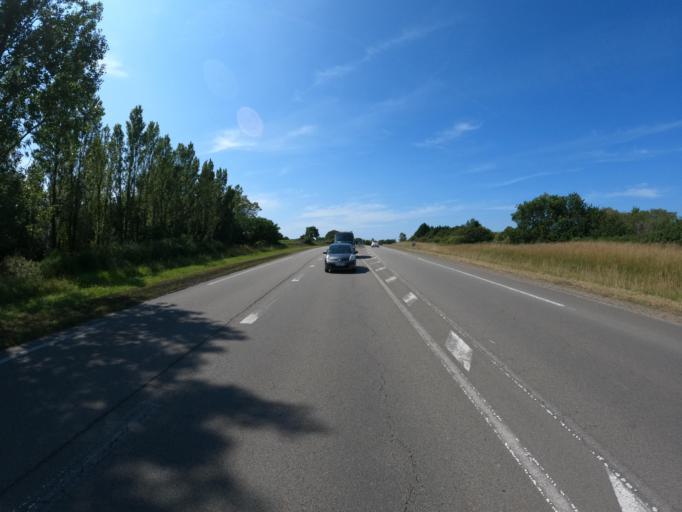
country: FR
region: Pays de la Loire
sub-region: Departement de la Loire-Atlantique
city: La Bernerie-en-Retz
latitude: 47.0890
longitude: -2.0306
